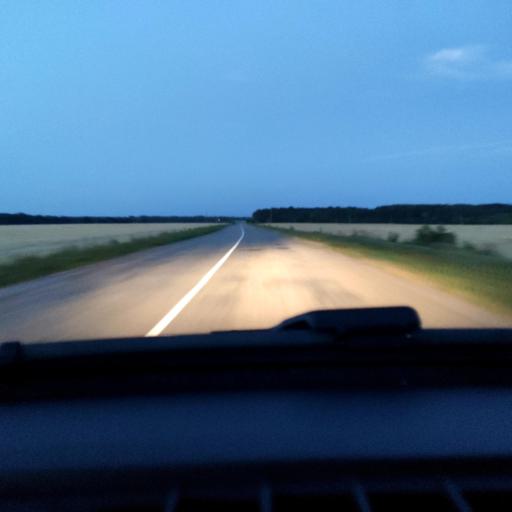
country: RU
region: Lipetsk
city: Zadonsk
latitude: 52.2977
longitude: 38.8147
